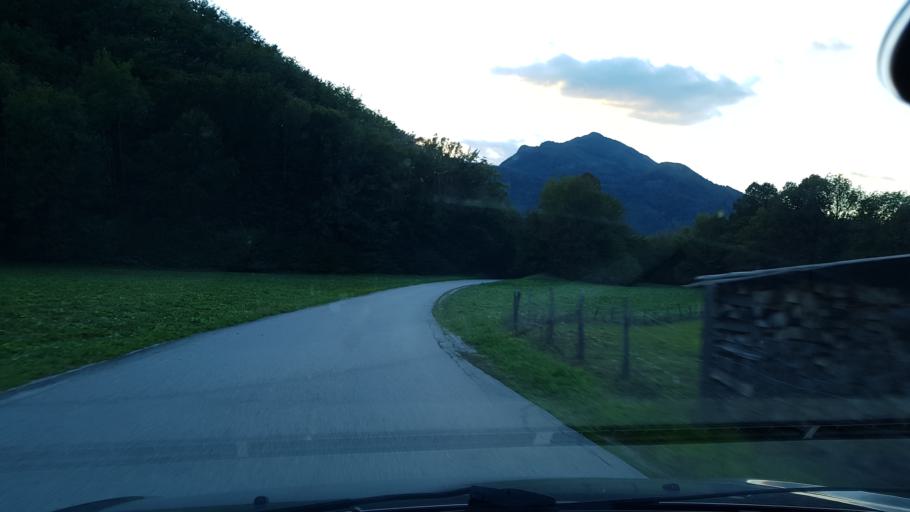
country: SI
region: Kobarid
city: Kobarid
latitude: 46.2583
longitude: 13.6001
